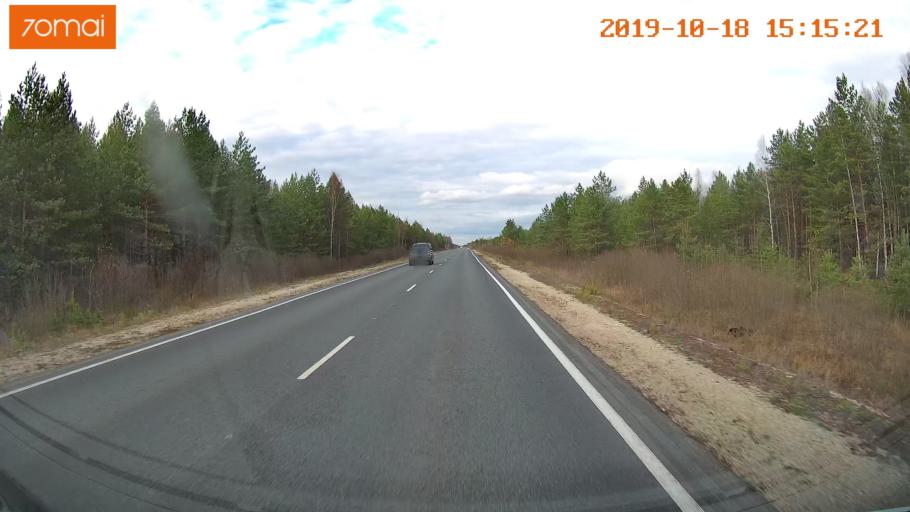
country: RU
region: Vladimir
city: Gus'-Khrustal'nyy
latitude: 55.6176
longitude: 40.7223
